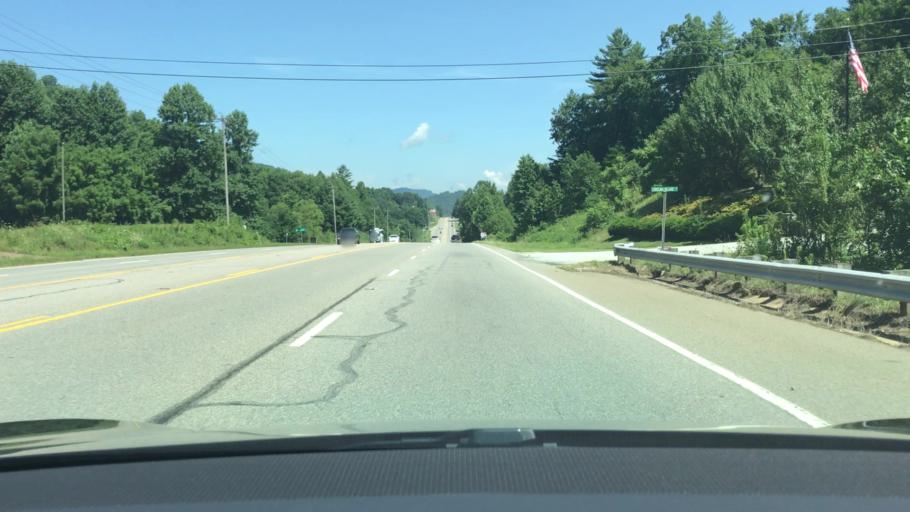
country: US
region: North Carolina
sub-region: Macon County
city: Franklin
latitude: 35.1063
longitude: -83.3869
